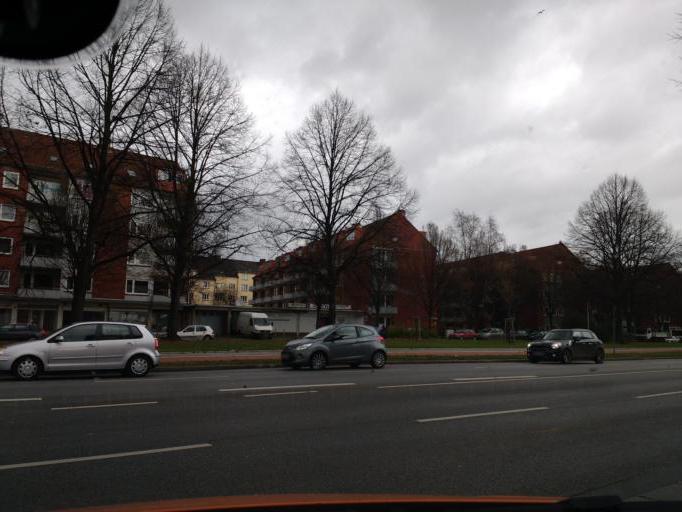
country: DE
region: Hamburg
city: Rothenburgsort
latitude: 53.5507
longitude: 10.0602
